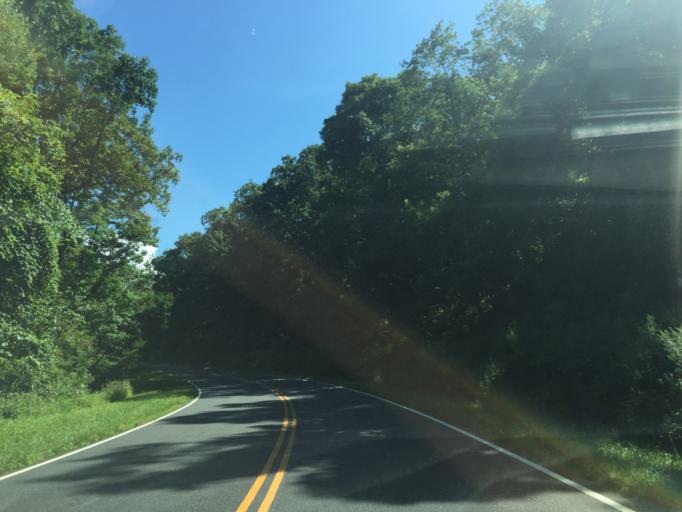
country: US
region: Virginia
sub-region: Page County
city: Luray
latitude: 38.7038
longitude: -78.3207
